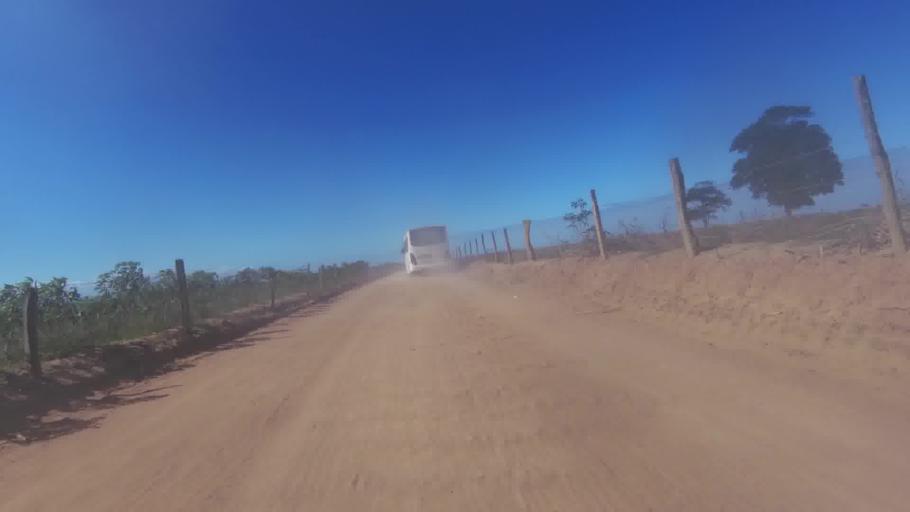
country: BR
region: Espirito Santo
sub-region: Marataizes
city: Marataizes
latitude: -21.1298
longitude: -40.9833
